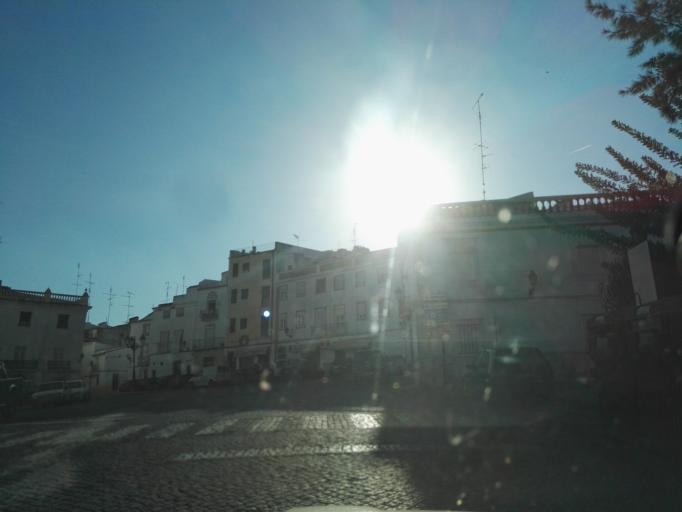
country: PT
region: Portalegre
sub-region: Elvas
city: Elvas
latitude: 38.8796
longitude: -7.1602
